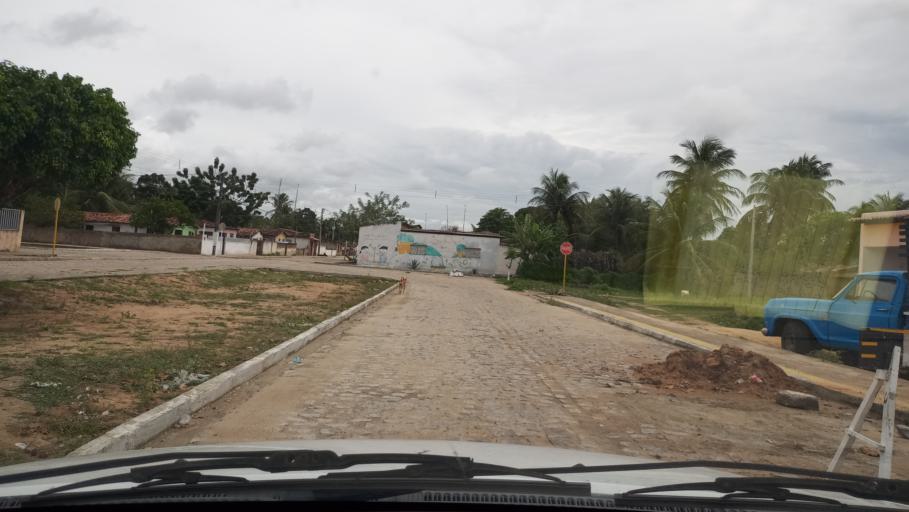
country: BR
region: Rio Grande do Norte
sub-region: Poco Branco
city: Poco Branco
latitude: -5.6187
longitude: -35.6595
